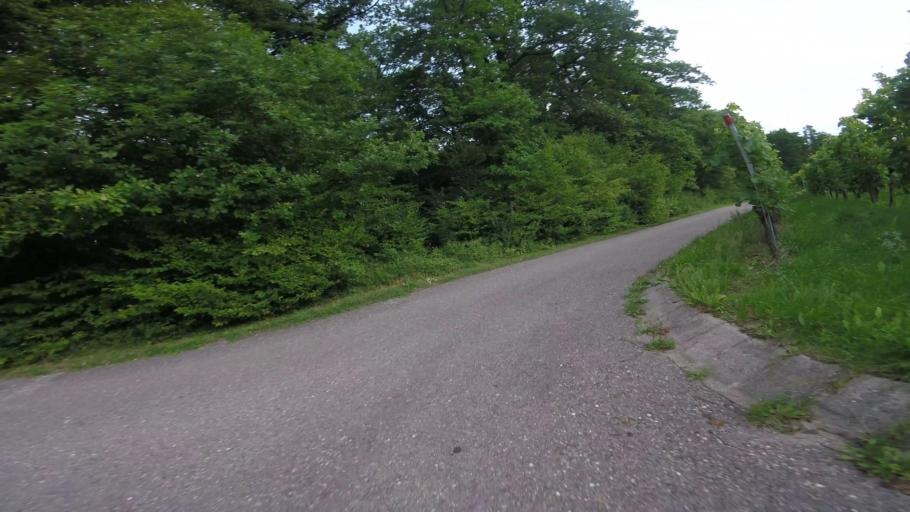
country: DE
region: Baden-Wuerttemberg
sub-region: Regierungsbezirk Stuttgart
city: Grossbottwar
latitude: 48.9925
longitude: 9.3198
